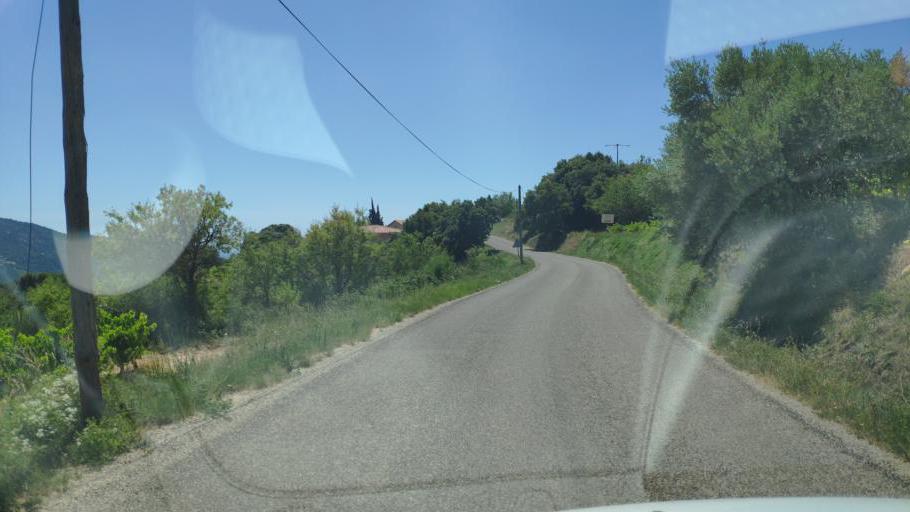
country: FR
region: Provence-Alpes-Cote d'Azur
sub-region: Departement du Vaucluse
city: Malaucene
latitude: 44.1734
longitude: 5.0742
